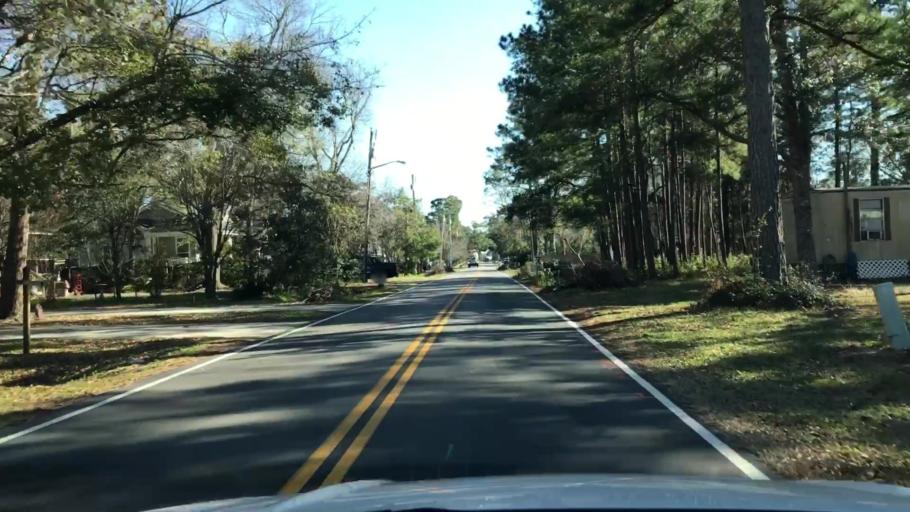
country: US
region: South Carolina
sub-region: Horry County
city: Garden City
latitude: 33.5927
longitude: -78.9995
